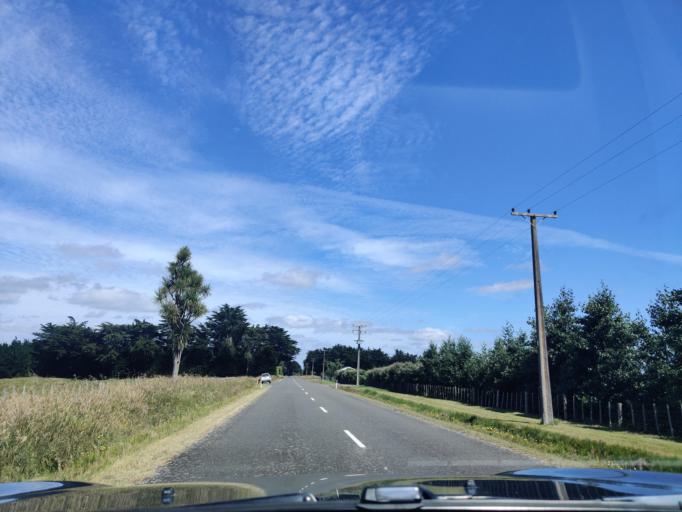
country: NZ
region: Manawatu-Wanganui
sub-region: Rangitikei District
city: Bulls
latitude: -40.1902
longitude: 175.4623
